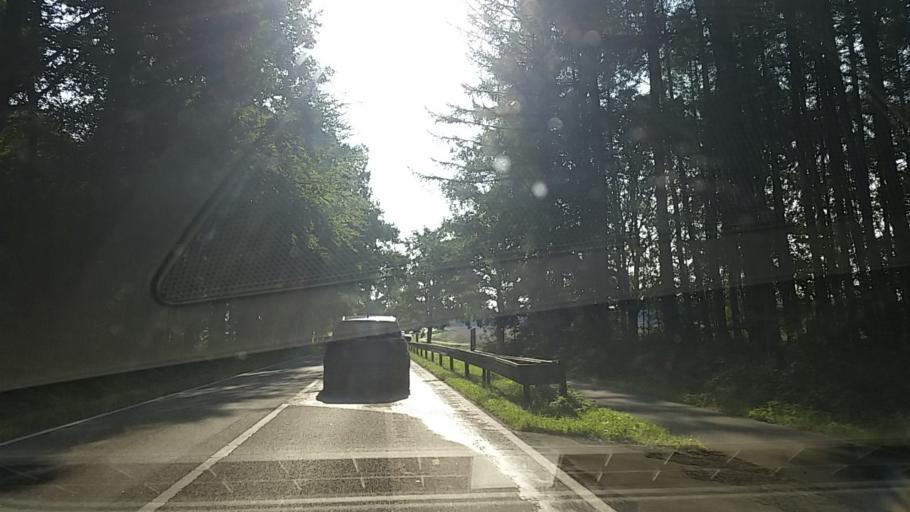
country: DE
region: Mecklenburg-Vorpommern
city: Wittenburg
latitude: 53.4821
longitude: 11.1190
